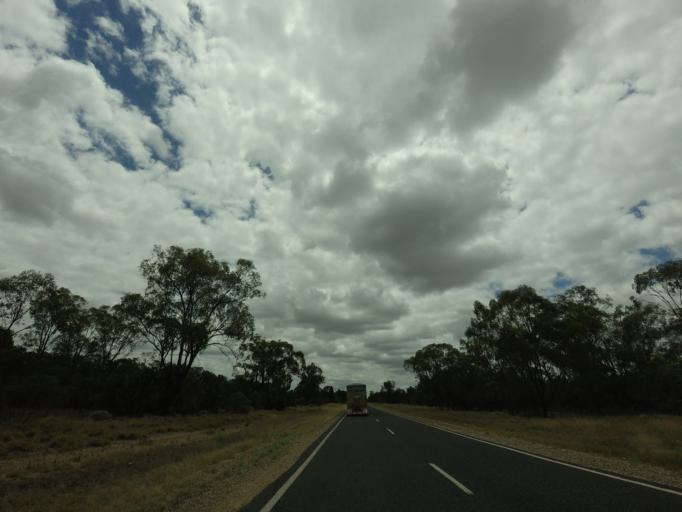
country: AU
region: Queensland
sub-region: Goondiwindi
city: Goondiwindi
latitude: -28.4295
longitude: 150.3022
